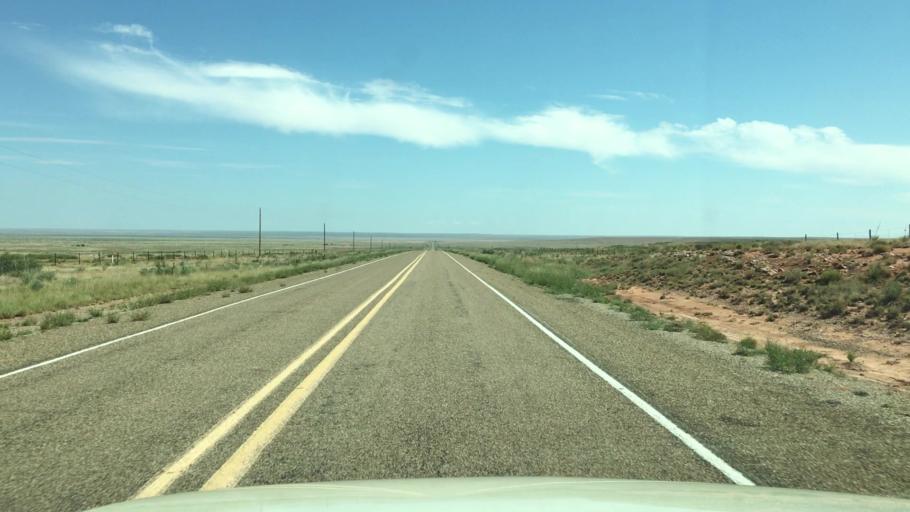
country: US
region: New Mexico
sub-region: Chaves County
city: Roswell
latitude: 33.9758
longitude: -104.5770
